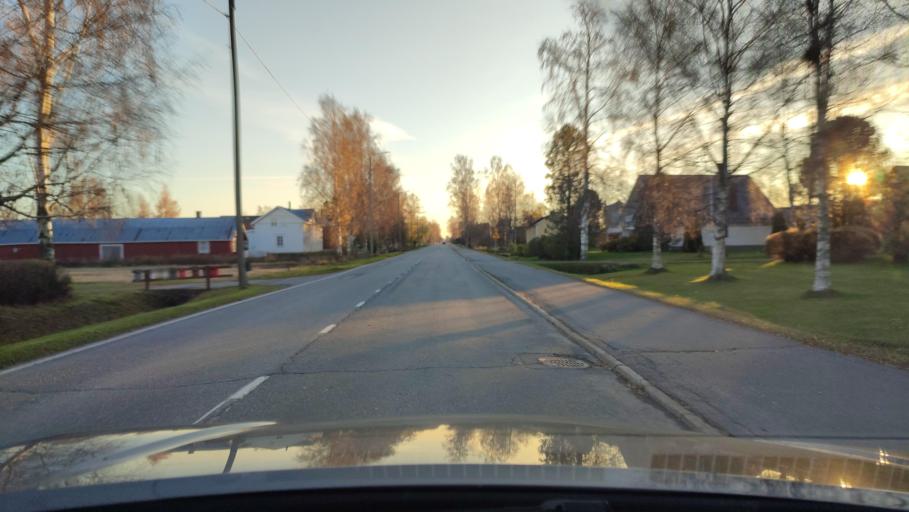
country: FI
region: Ostrobothnia
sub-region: Sydosterbotten
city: Naerpes
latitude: 62.5468
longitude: 21.3984
